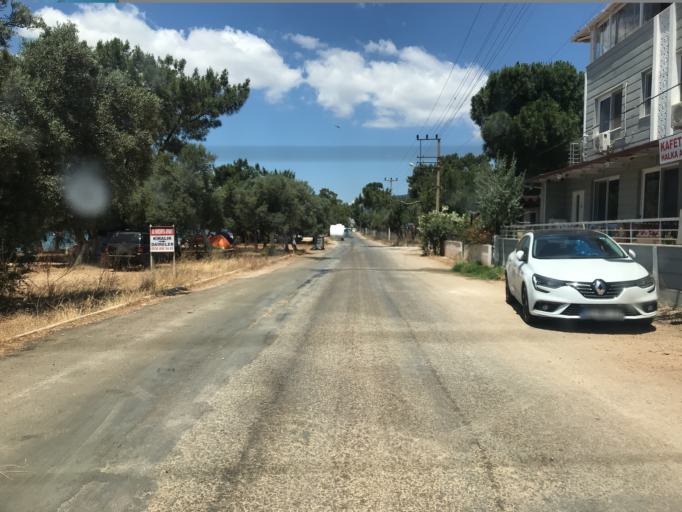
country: TR
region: Aydin
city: Sarikemer
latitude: 37.4062
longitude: 27.4268
